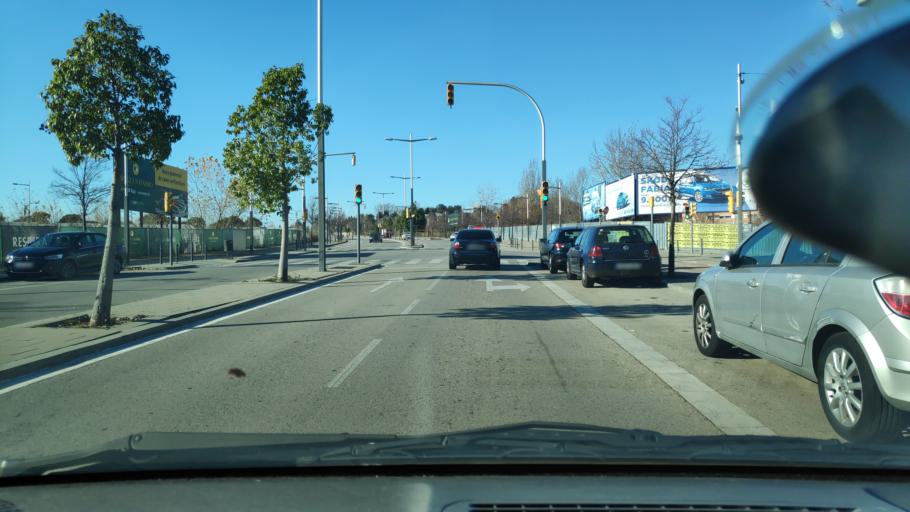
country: ES
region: Catalonia
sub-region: Provincia de Barcelona
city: Sant Quirze del Valles
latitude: 41.5407
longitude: 2.0887
